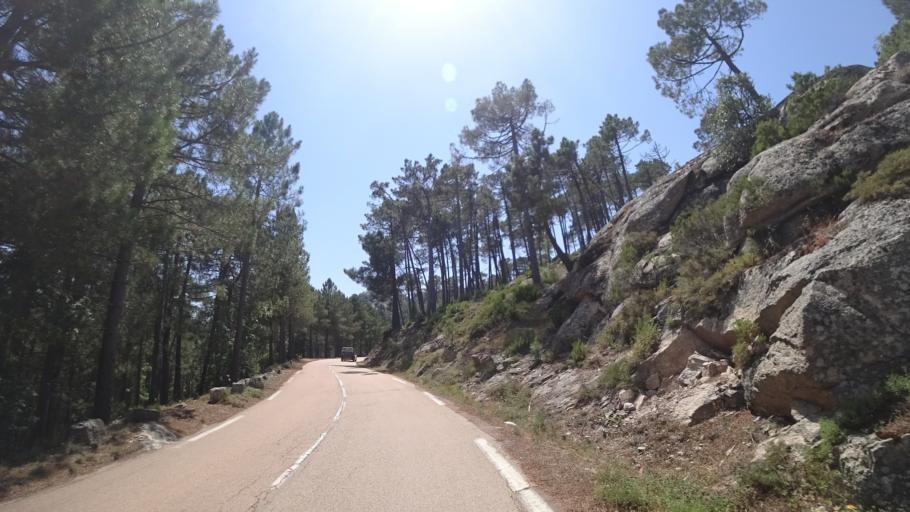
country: FR
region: Corsica
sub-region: Departement de la Corse-du-Sud
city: Zonza
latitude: 41.6801
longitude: 9.2030
